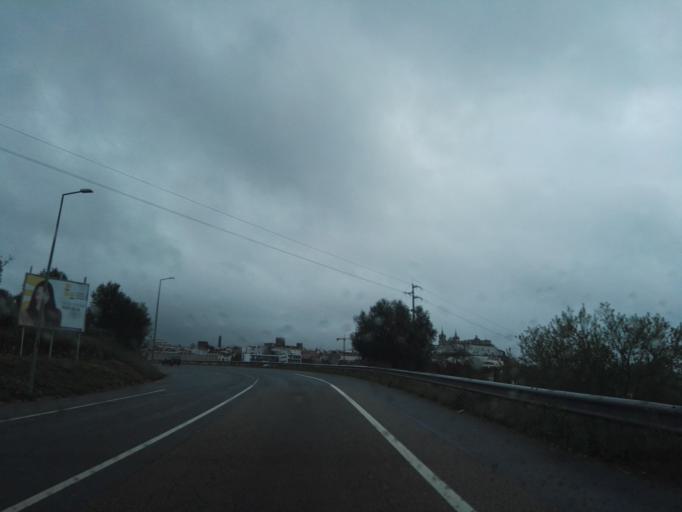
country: PT
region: Portalegre
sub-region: Portalegre
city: Portalegre
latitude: 39.2972
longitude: -7.4359
